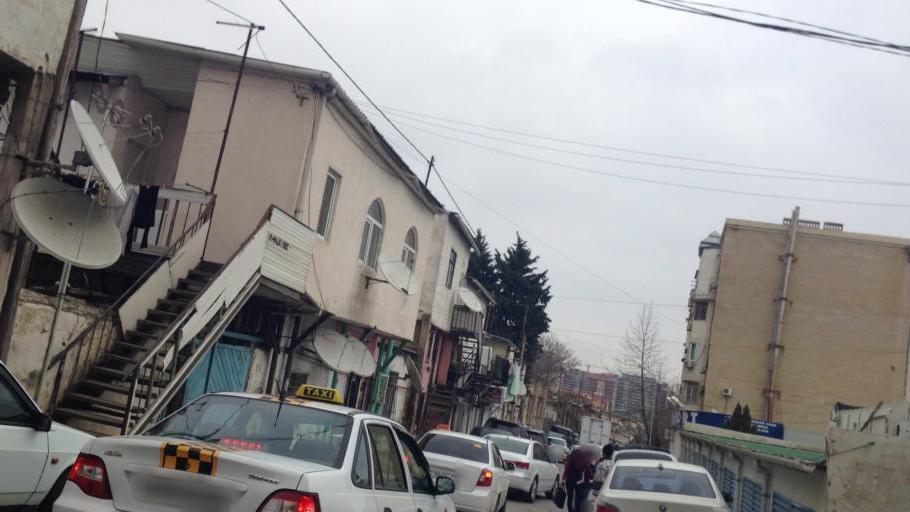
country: AZ
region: Baki
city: Badamdar
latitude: 40.3809
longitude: 49.8259
